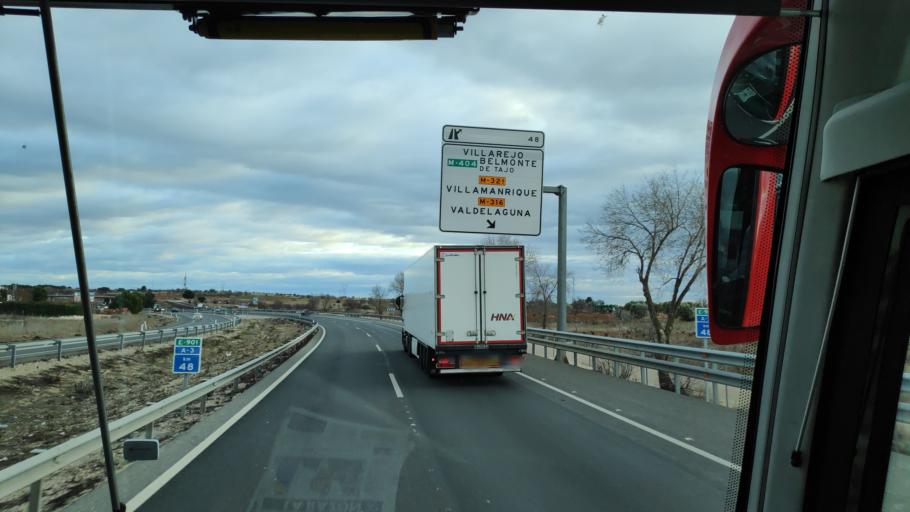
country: ES
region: Madrid
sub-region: Provincia de Madrid
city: Villarejo de Salvanes
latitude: 40.1757
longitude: -3.2957
